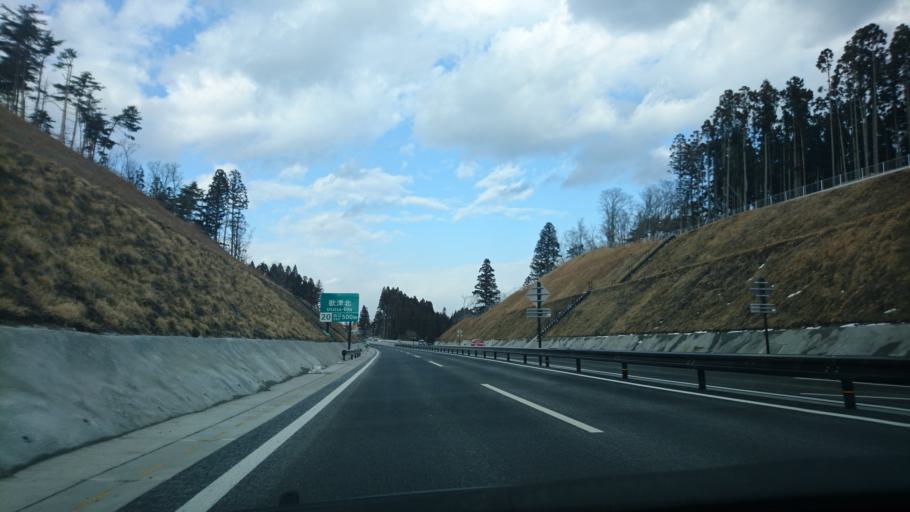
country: JP
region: Miyagi
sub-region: Oshika Gun
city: Onagawa Cho
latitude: 38.7356
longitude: 141.5216
